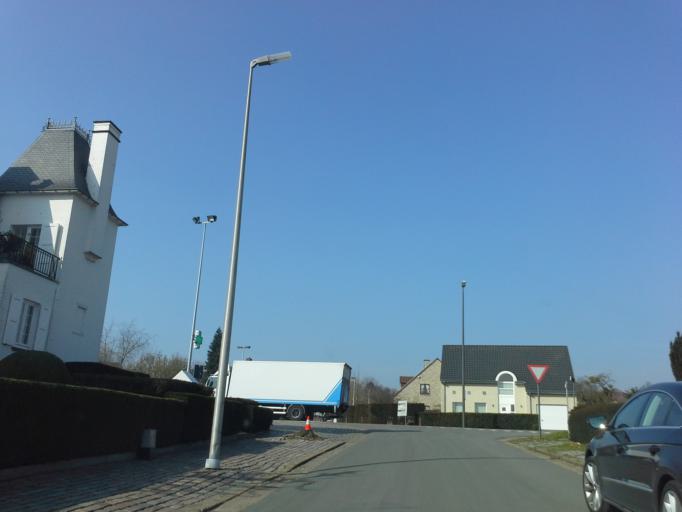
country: BE
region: Flanders
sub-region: Provincie Limburg
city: Hoeselt
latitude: 50.8466
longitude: 5.4887
